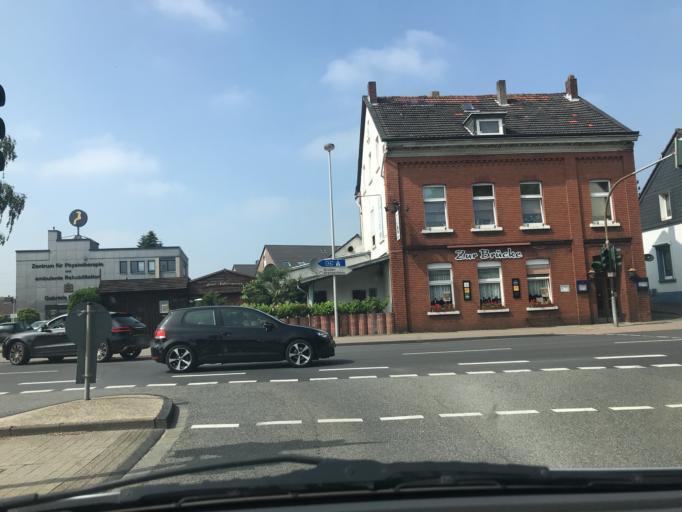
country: DE
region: North Rhine-Westphalia
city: Haan
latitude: 51.1927
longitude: 6.9973
